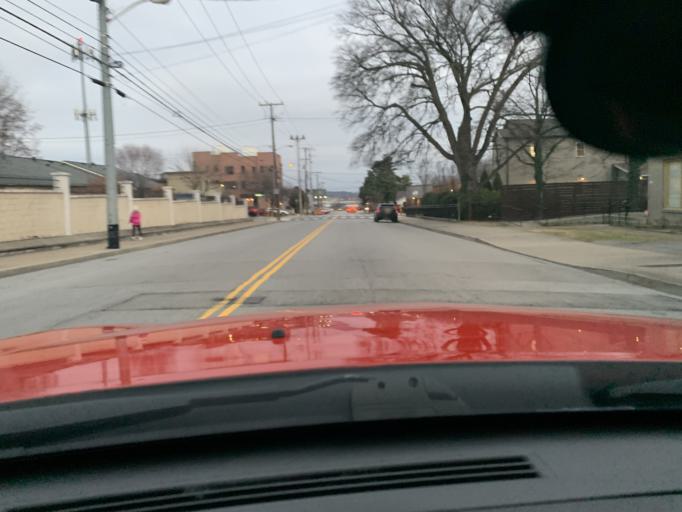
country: US
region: Tennessee
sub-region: Davidson County
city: Nashville
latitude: 36.1537
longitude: -86.7658
